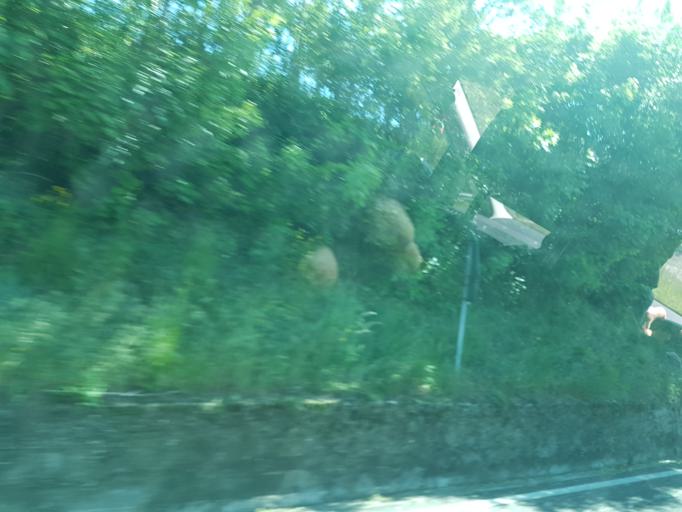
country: IT
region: Veneto
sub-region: Provincia di Vicenza
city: Pianezze
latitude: 45.7688
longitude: 11.6368
